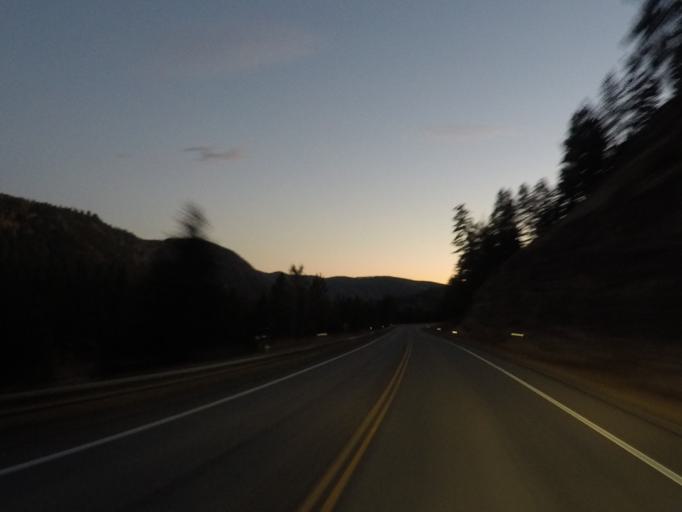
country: US
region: Montana
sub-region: Missoula County
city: Seeley Lake
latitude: 47.0194
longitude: -113.3193
